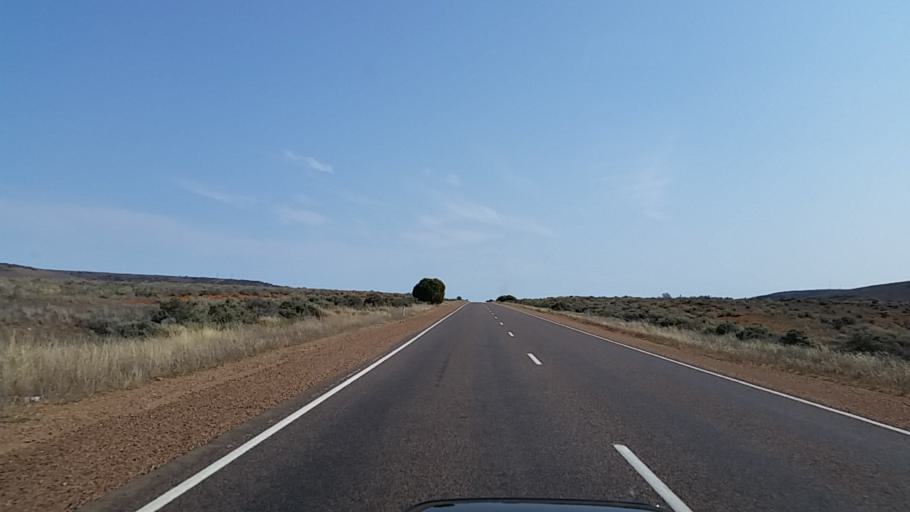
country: AU
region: South Australia
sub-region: Port Augusta
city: Port Augusta West
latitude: -32.5884
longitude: 137.6116
